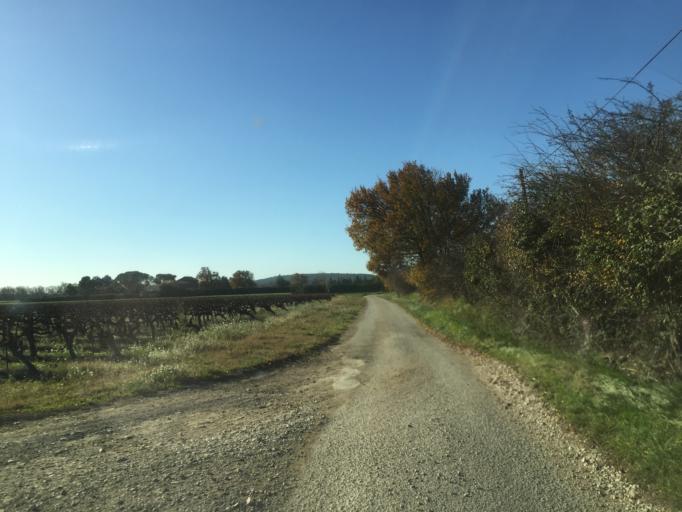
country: FR
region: Provence-Alpes-Cote d'Azur
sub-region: Departement du Vaucluse
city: Bedarrides
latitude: 44.0465
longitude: 4.9259
